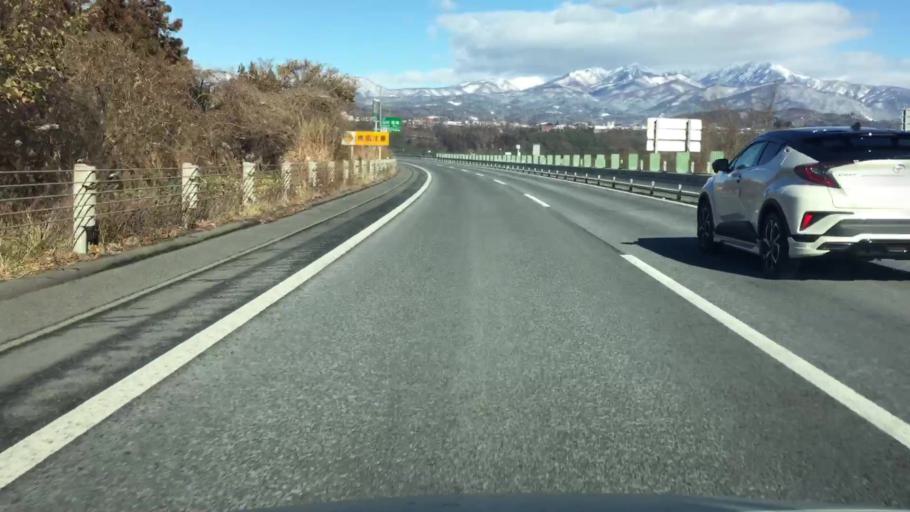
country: JP
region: Gunma
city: Numata
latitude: 36.6429
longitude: 139.0796
